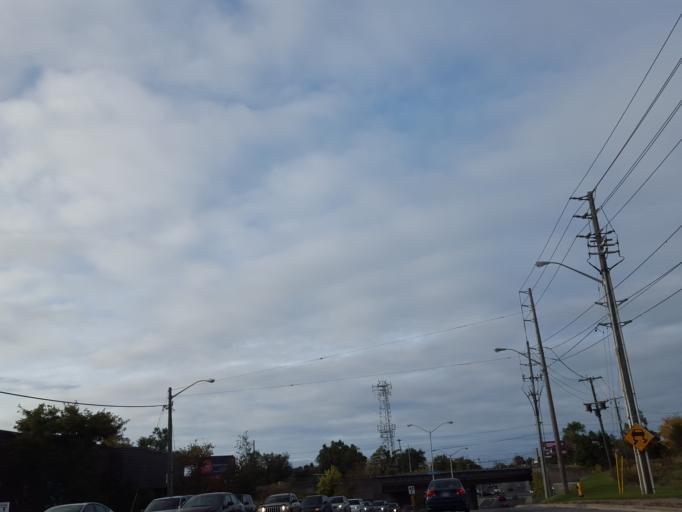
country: CA
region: Ontario
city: Scarborough
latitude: 43.7590
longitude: -79.3002
